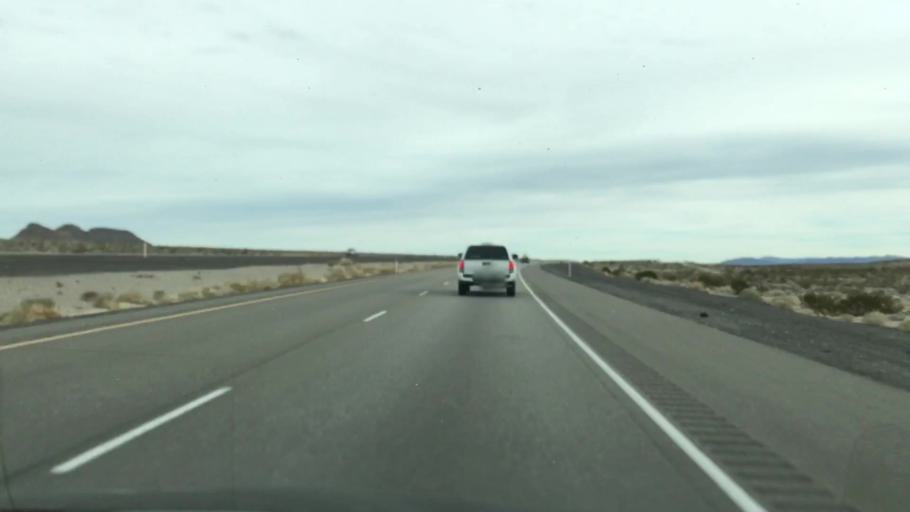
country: US
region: Nevada
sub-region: Nye County
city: Pahrump
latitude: 36.6011
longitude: -115.9683
